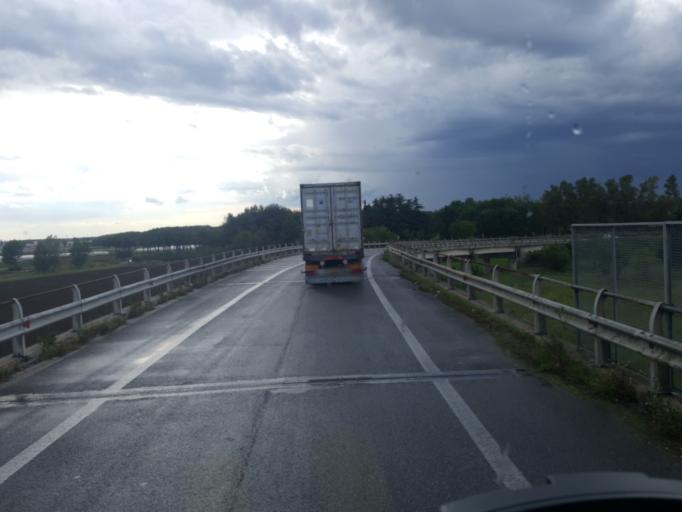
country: IT
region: Campania
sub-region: Provincia di Napoli
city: Pascarola
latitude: 40.9917
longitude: 14.2937
